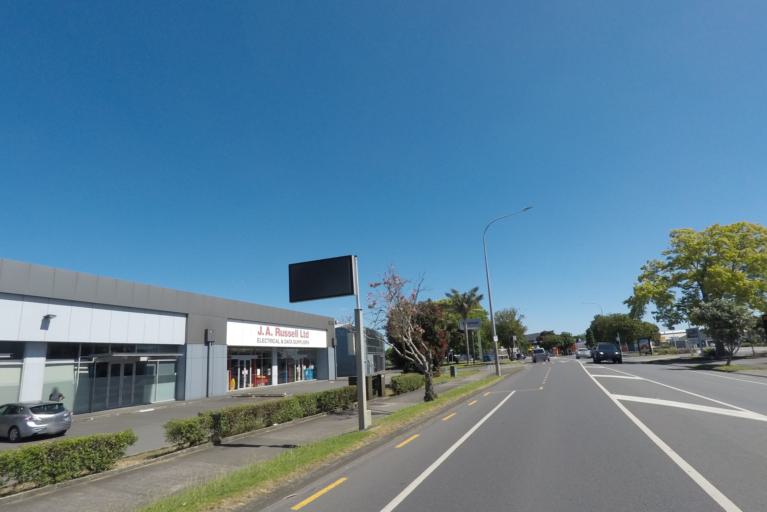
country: NZ
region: Auckland
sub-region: Auckland
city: Rosebank
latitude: -36.8736
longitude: 174.6696
